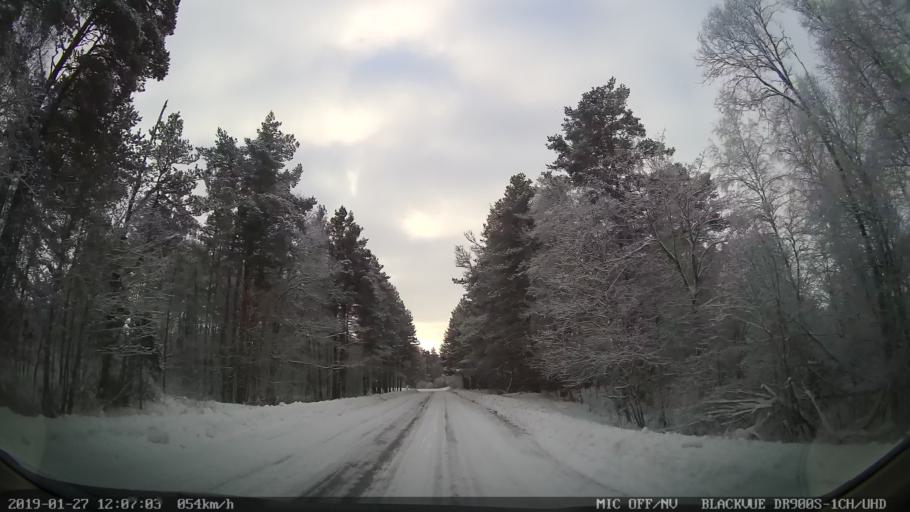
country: EE
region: Harju
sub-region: Raasiku vald
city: Raasiku
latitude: 59.4666
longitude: 25.2398
